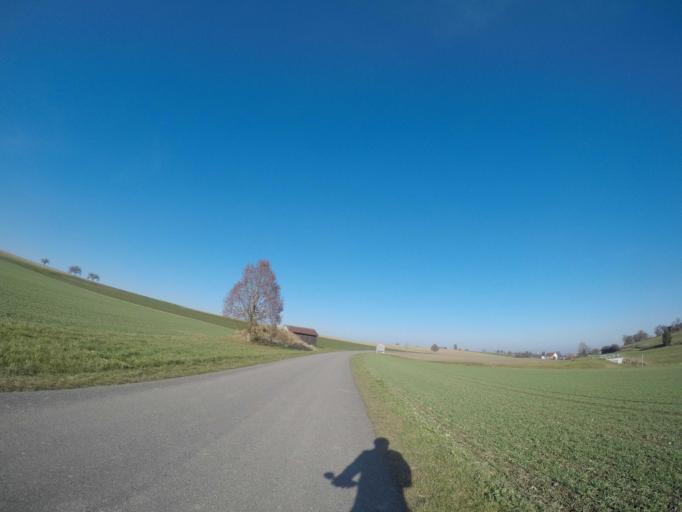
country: DE
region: Baden-Wuerttemberg
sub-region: Tuebingen Region
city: Unterwachingen
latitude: 48.2114
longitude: 9.6464
